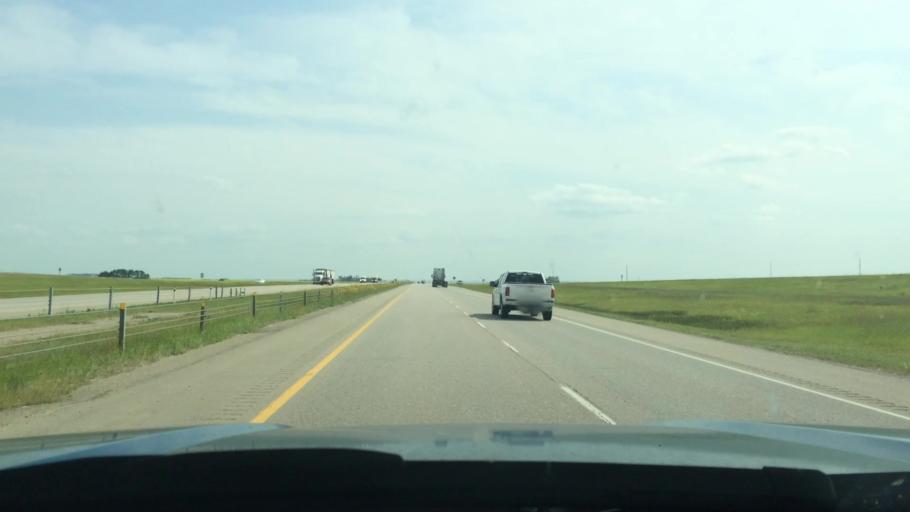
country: CA
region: Alberta
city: Didsbury
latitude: 51.6639
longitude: -114.0256
